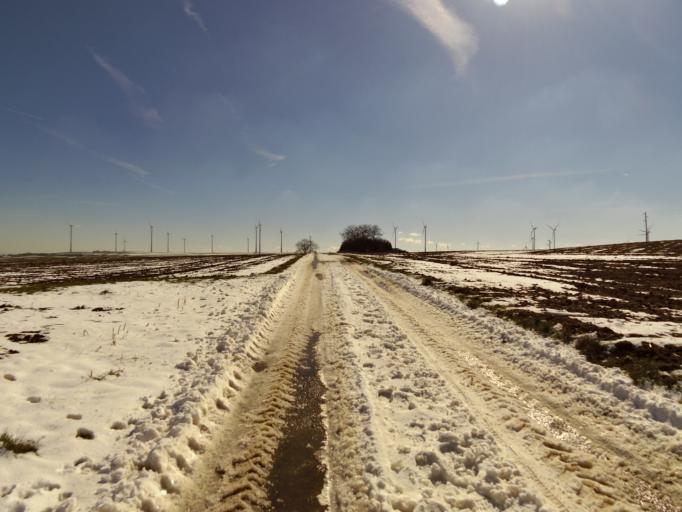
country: DE
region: Rheinland-Pfalz
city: Immesheim
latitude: 49.6346
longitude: 8.1089
